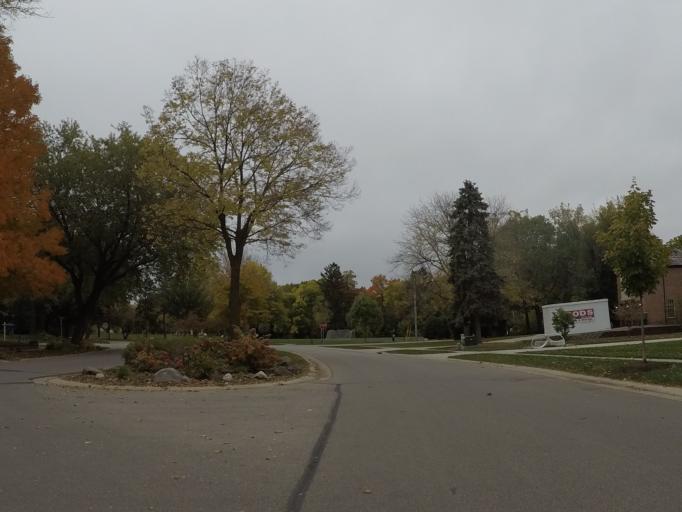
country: US
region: Wisconsin
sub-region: Dane County
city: Maple Bluff
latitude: 43.1055
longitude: -89.3667
